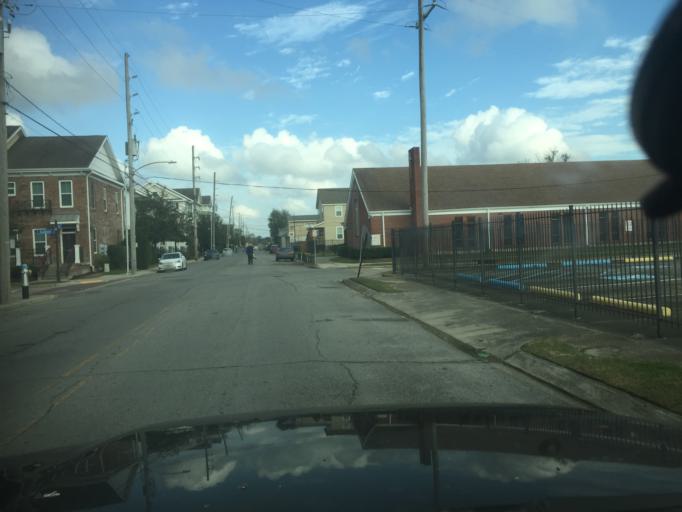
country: US
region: Louisiana
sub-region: Orleans Parish
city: New Orleans
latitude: 29.9938
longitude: -90.0772
